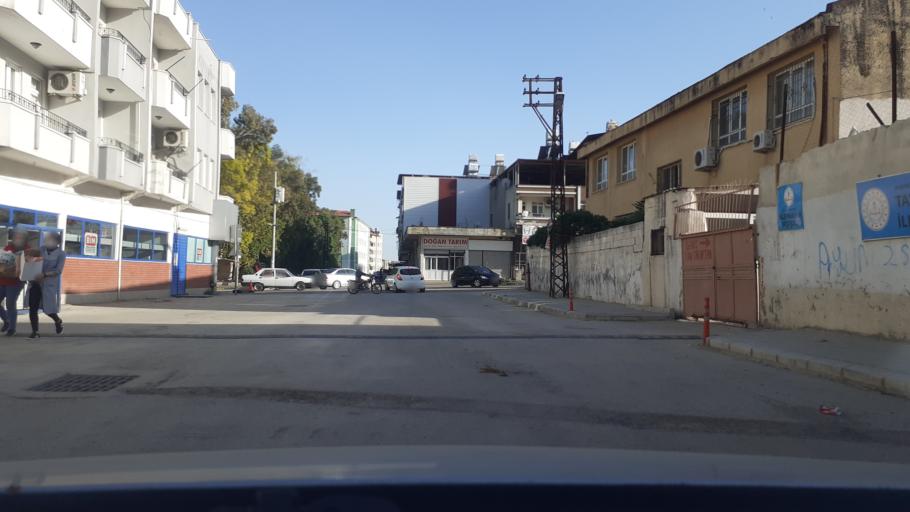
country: TR
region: Hatay
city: Kirikhan
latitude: 36.4997
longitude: 36.3651
